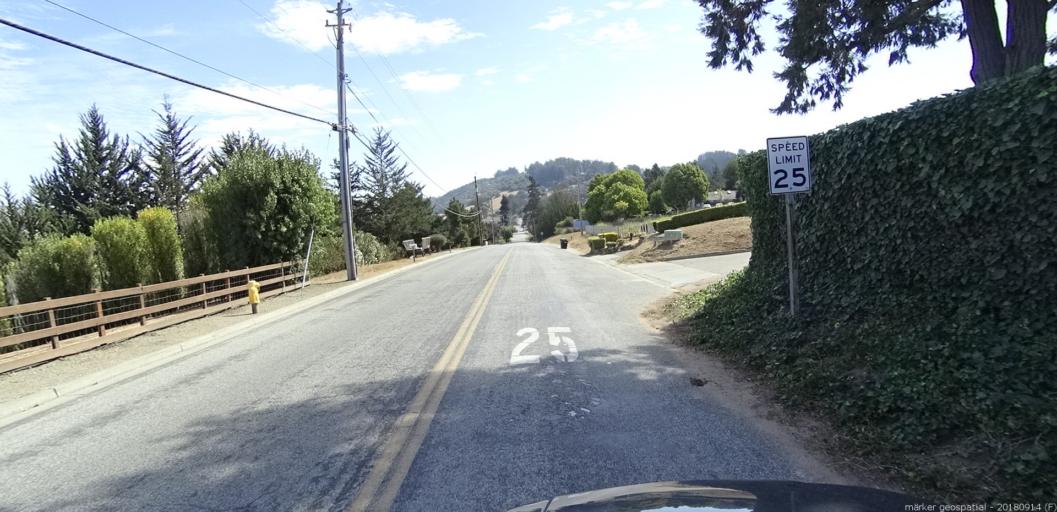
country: US
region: California
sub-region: San Benito County
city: Aromas
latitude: 36.8879
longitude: -121.6489
